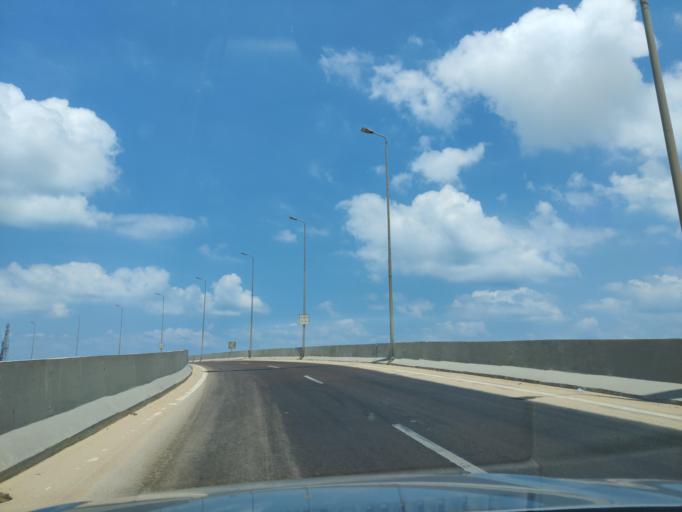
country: EG
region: Alexandria
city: Alexandria
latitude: 31.0132
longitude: 29.6339
